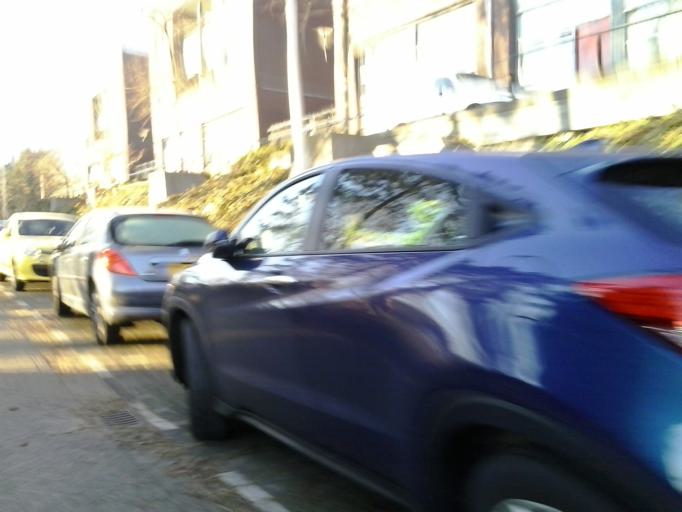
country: NL
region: South Holland
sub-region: Gemeente Lansingerland
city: Bergschenhoek
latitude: 51.9883
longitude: 4.5017
